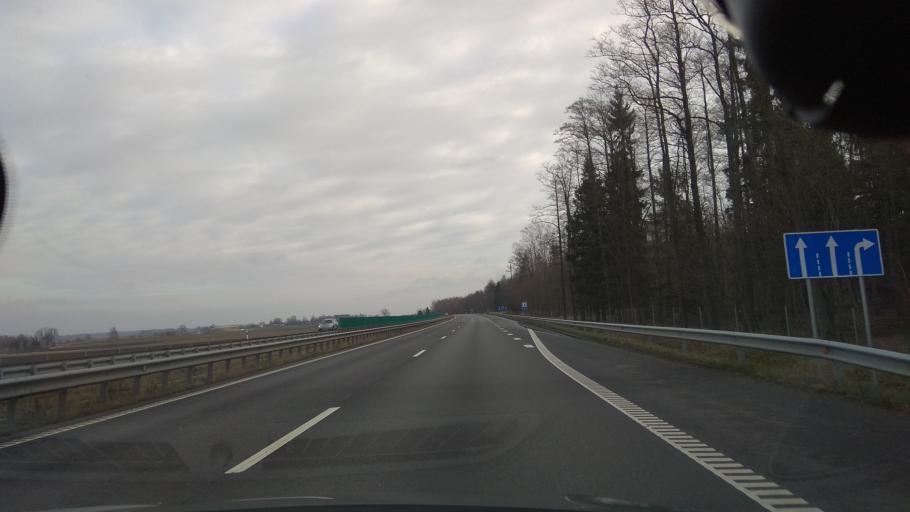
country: LT
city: Kazlu Ruda
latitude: 54.6760
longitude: 23.5597
